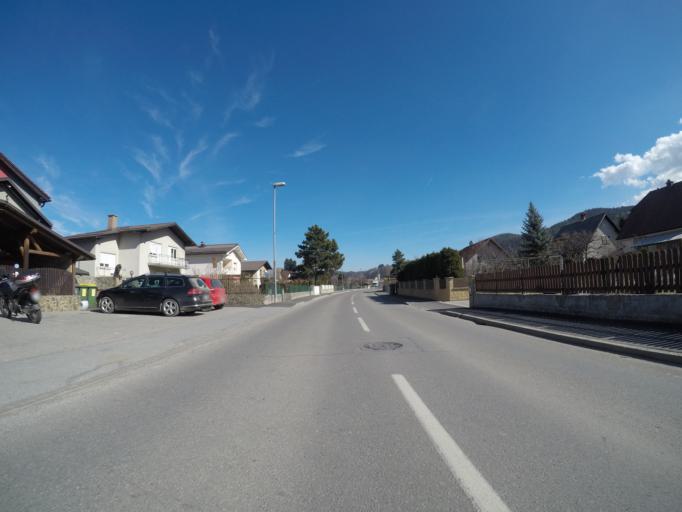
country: SI
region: Selnica ob Dravi
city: Selnica ob Dravi
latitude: 46.5370
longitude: 15.4993
